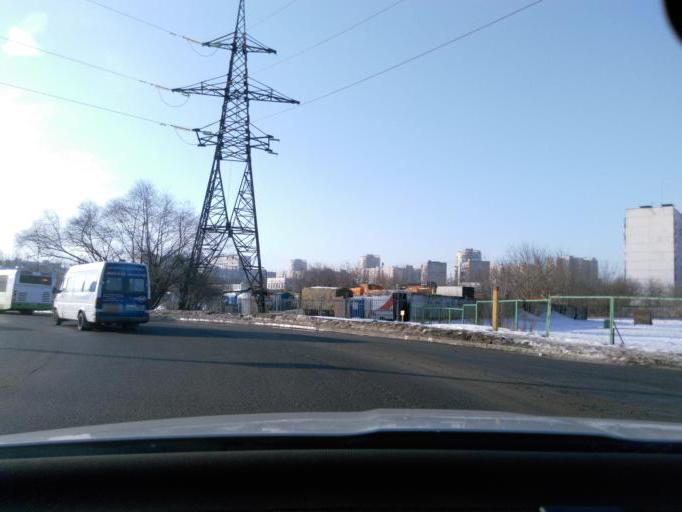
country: RU
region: Moskovskaya
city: Levoberezhnaya
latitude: 55.8764
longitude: 37.4692
